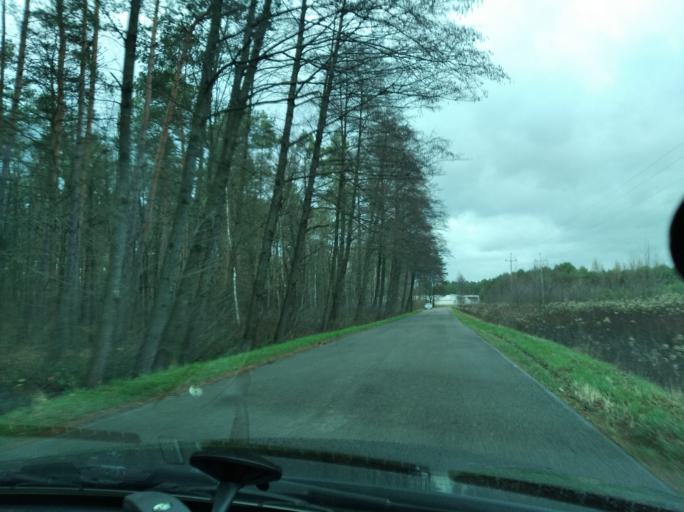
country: PL
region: Subcarpathian Voivodeship
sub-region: Powiat lancucki
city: Zolynia
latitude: 50.1321
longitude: 22.2829
